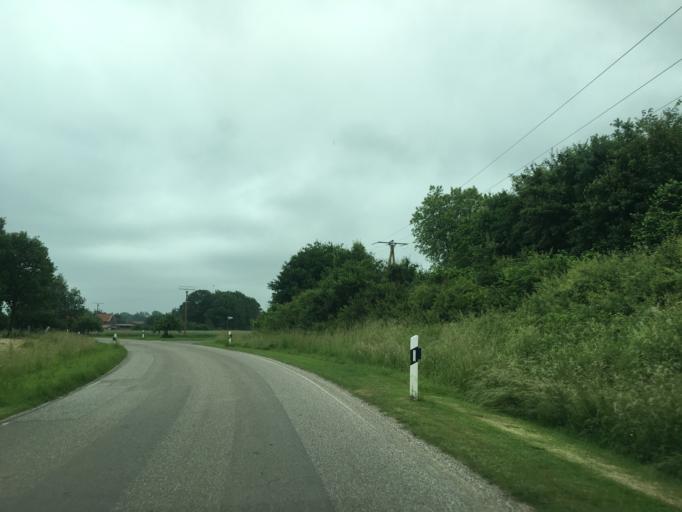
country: DE
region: North Rhine-Westphalia
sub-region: Regierungsbezirk Munster
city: Altenberge
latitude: 52.0215
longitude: 7.4603
